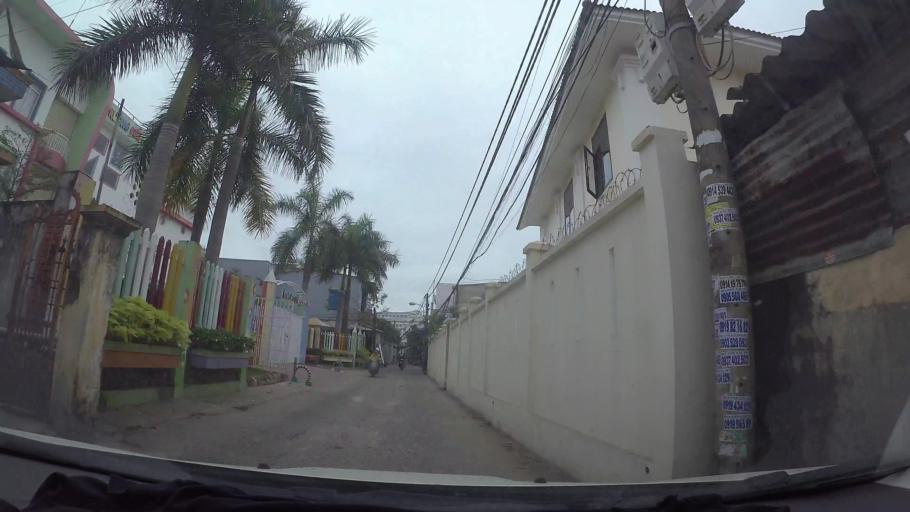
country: VN
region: Da Nang
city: Lien Chieu
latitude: 16.0733
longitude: 108.1443
